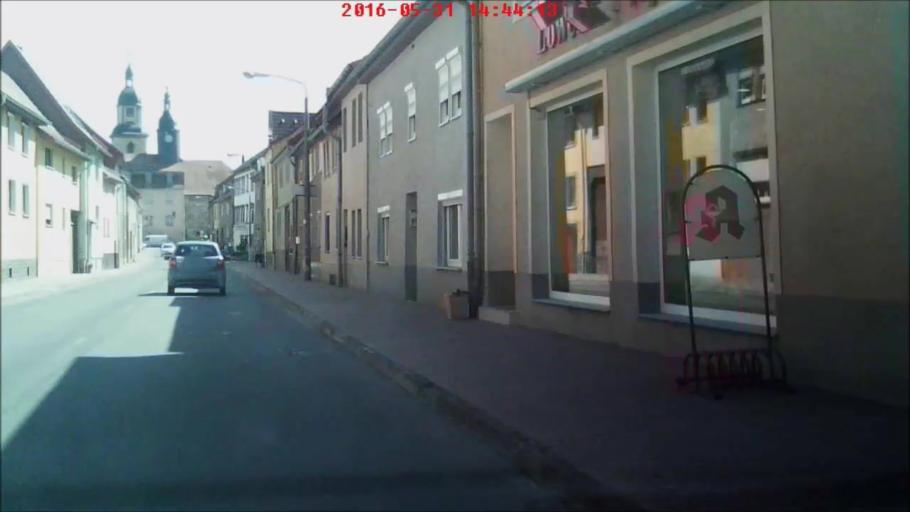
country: DE
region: Thuringia
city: Kindelbruck
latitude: 51.2634
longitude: 11.0911
